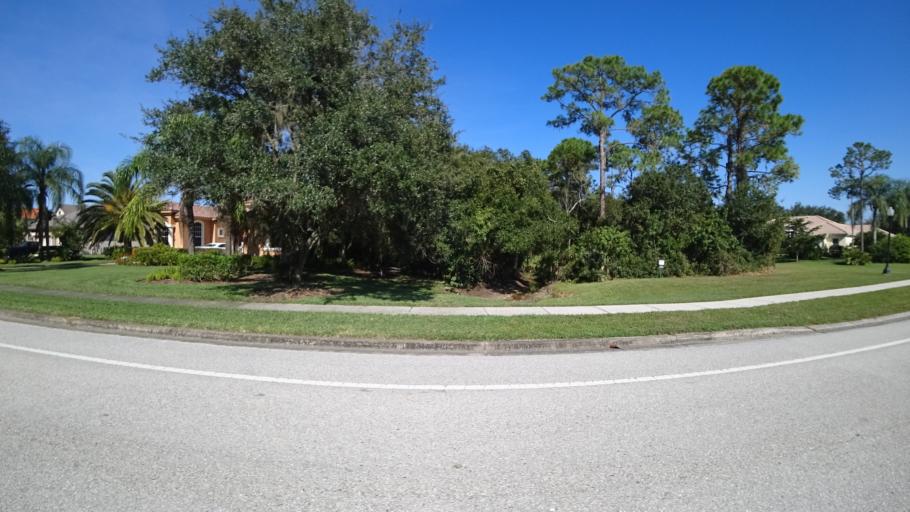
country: US
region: Florida
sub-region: Sarasota County
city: The Meadows
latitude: 27.4038
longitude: -82.4363
